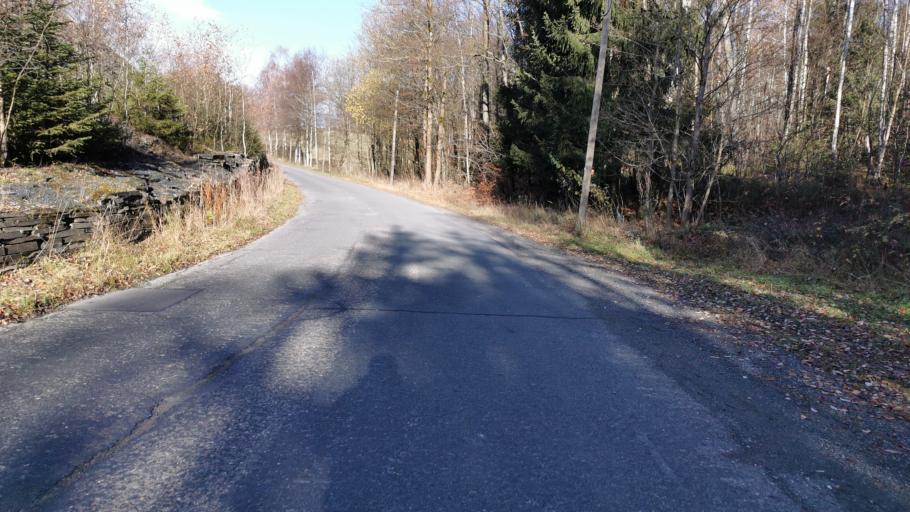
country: DE
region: Bavaria
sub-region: Upper Franconia
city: Reichenbach
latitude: 50.4648
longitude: 11.4397
